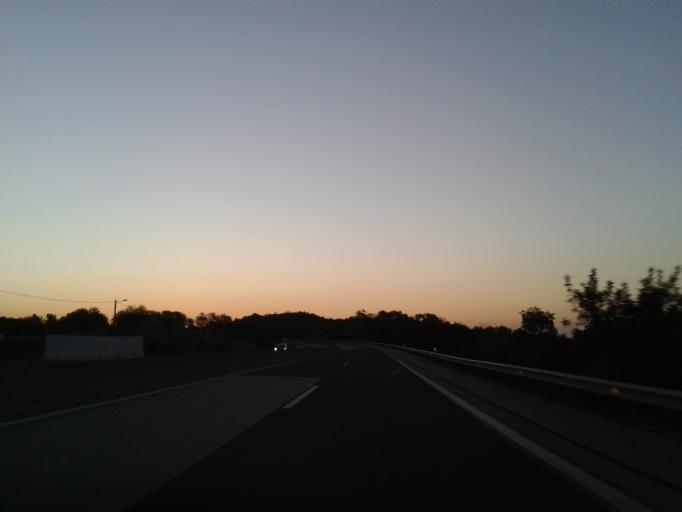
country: PT
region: Faro
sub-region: Loule
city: Boliqueime
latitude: 37.1505
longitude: -8.1694
